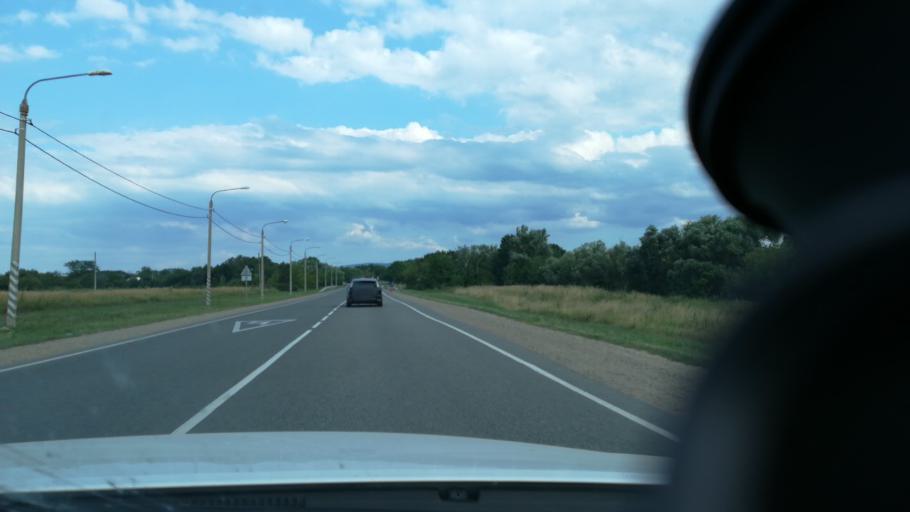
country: RU
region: Krasnodarskiy
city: Gostagayevskaya
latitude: 45.0324
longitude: 37.4887
